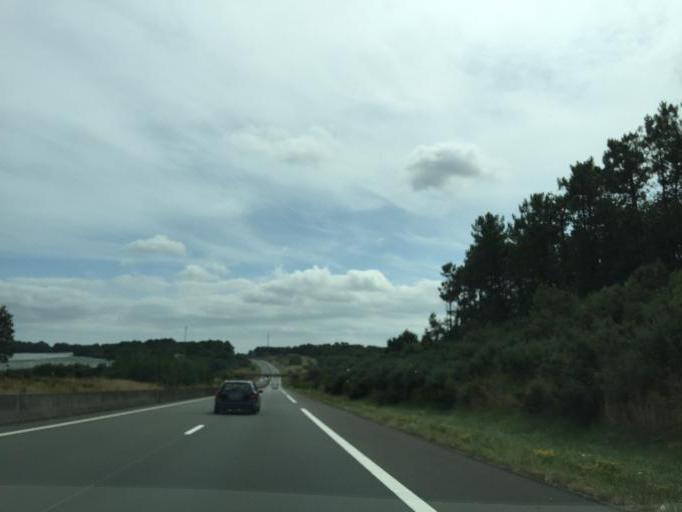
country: FR
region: Pays de la Loire
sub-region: Departement de la Sarthe
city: Luceau
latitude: 47.7171
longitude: 0.3451
